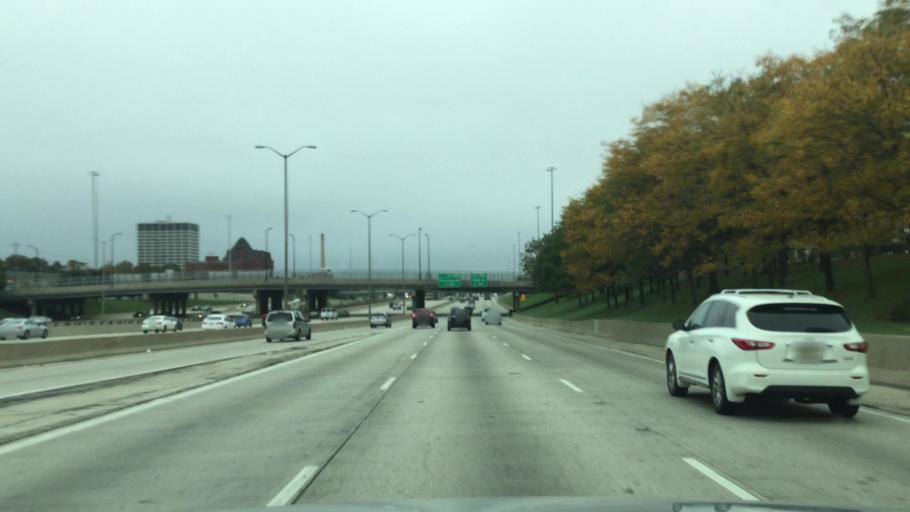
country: US
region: Illinois
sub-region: Cook County
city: Chicago
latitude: 41.8400
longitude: -87.6314
